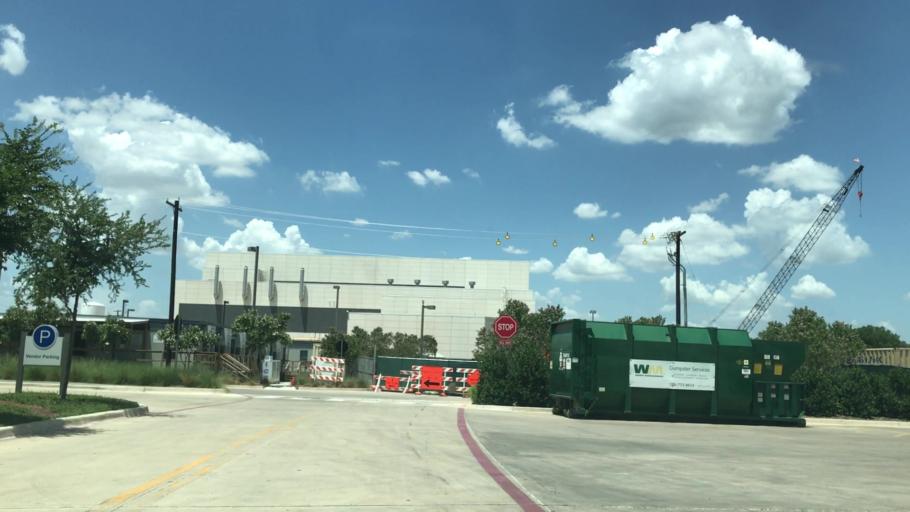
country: US
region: Texas
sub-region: Dallas County
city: Dallas
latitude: 32.8194
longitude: -96.8507
